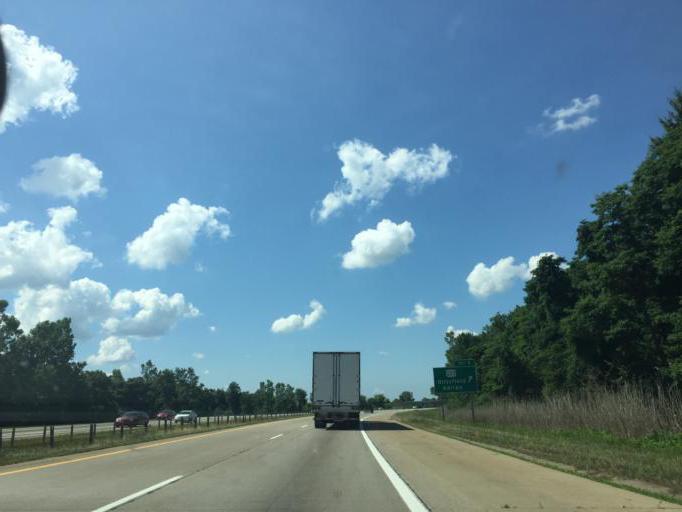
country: US
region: Michigan
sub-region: Monroe County
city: Lambertville
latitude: 41.8031
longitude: -83.6846
